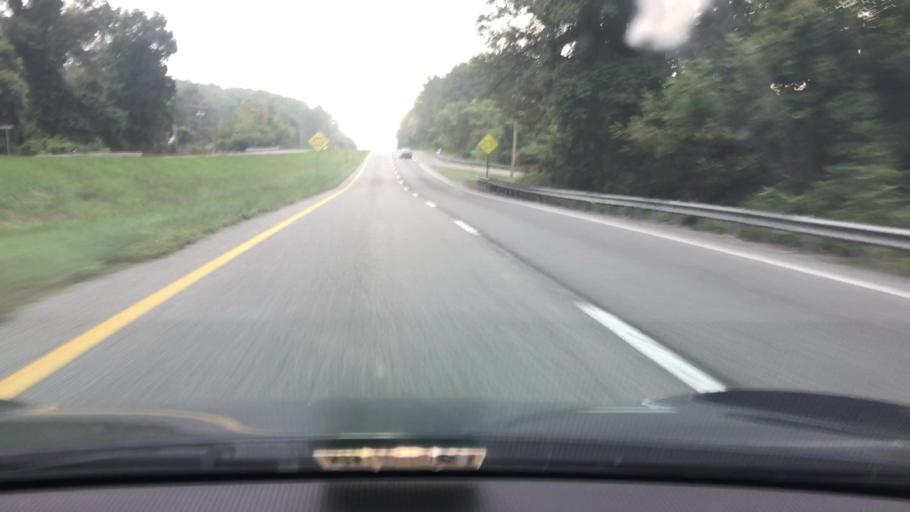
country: US
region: Virginia
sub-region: Botetourt County
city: Blue Ridge
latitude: 37.3957
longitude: -79.7743
